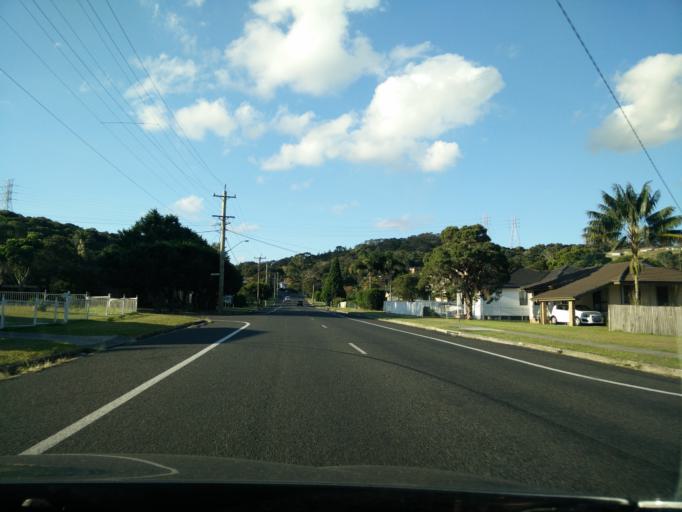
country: AU
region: New South Wales
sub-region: Wollongong
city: Berkeley
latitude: -34.4739
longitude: 150.8417
